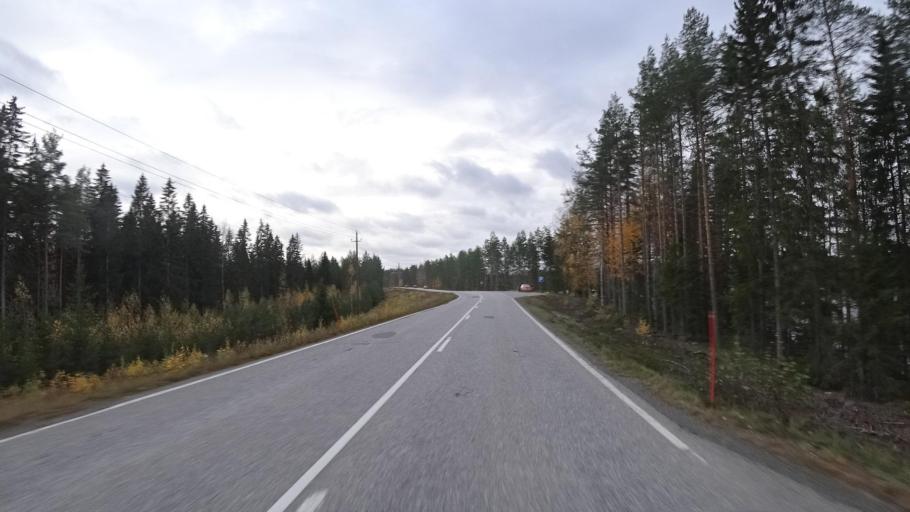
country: FI
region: Central Finland
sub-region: Joutsa
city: Joutsa
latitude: 61.7803
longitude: 26.1588
